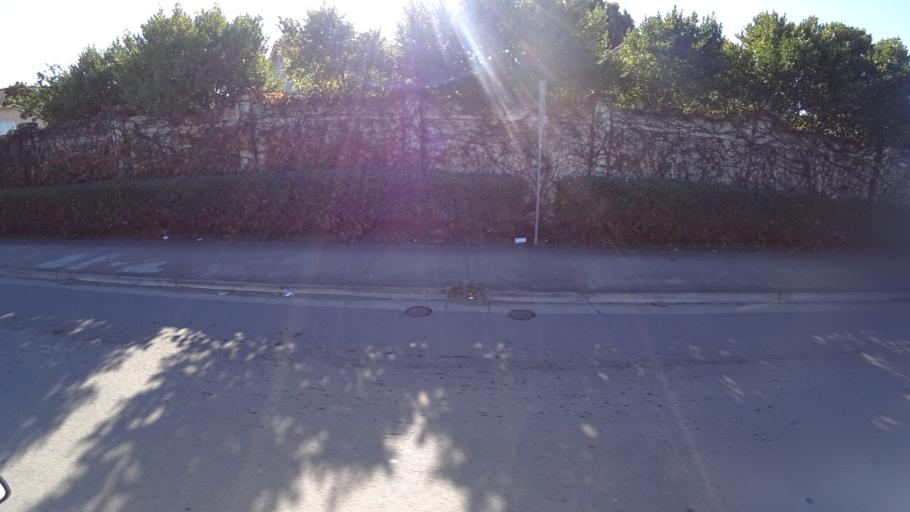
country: US
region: California
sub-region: Alameda County
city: Union City
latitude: 37.6059
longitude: -122.0319
